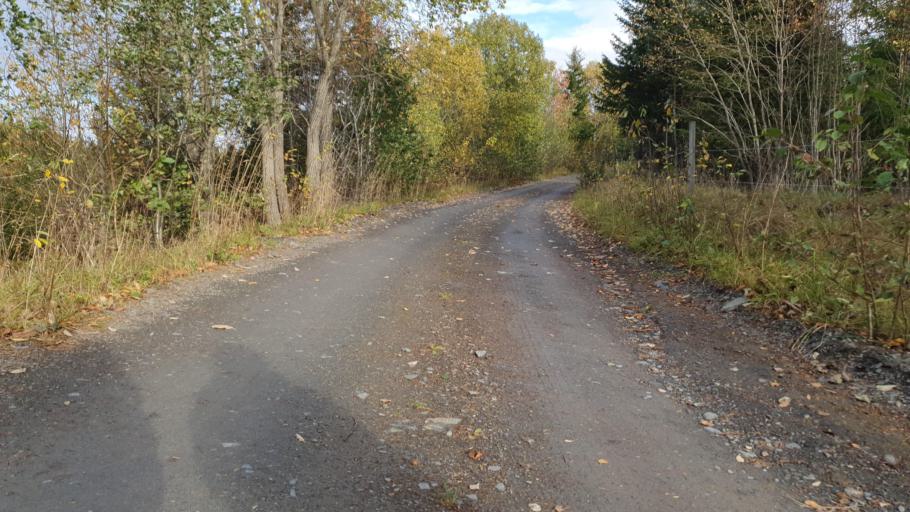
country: NO
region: Sor-Trondelag
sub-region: Klaebu
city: Klaebu
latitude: 63.2900
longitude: 10.4608
